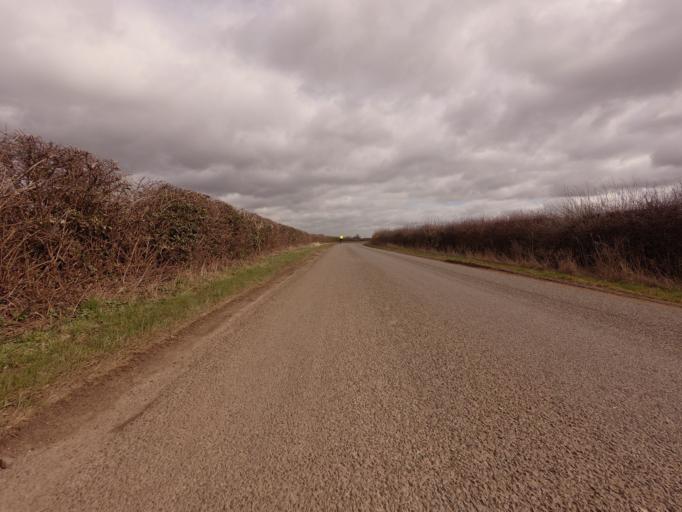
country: GB
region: England
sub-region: Lincolnshire
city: Barrowby
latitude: 52.8712
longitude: -0.6827
